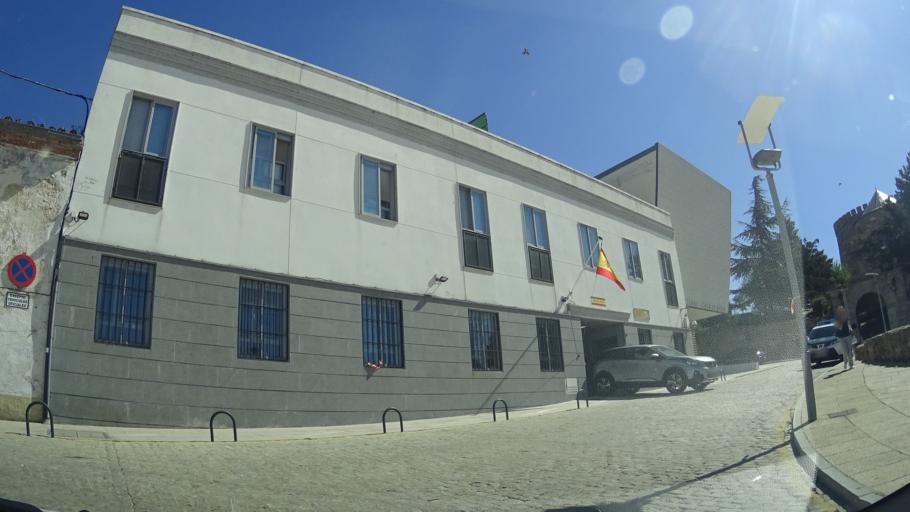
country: ES
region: Castille and Leon
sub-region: Provincia de Avila
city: Las Navas del Marques
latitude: 40.6040
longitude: -4.3268
